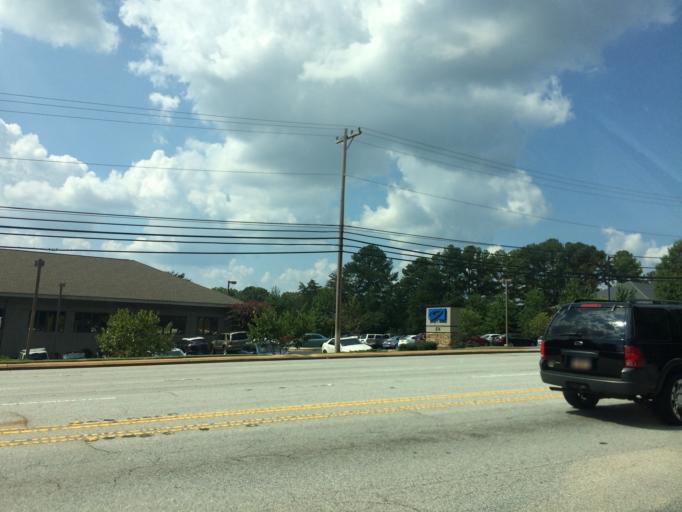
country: US
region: South Carolina
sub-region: Greenville County
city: Greenville
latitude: 34.8150
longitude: -82.3681
